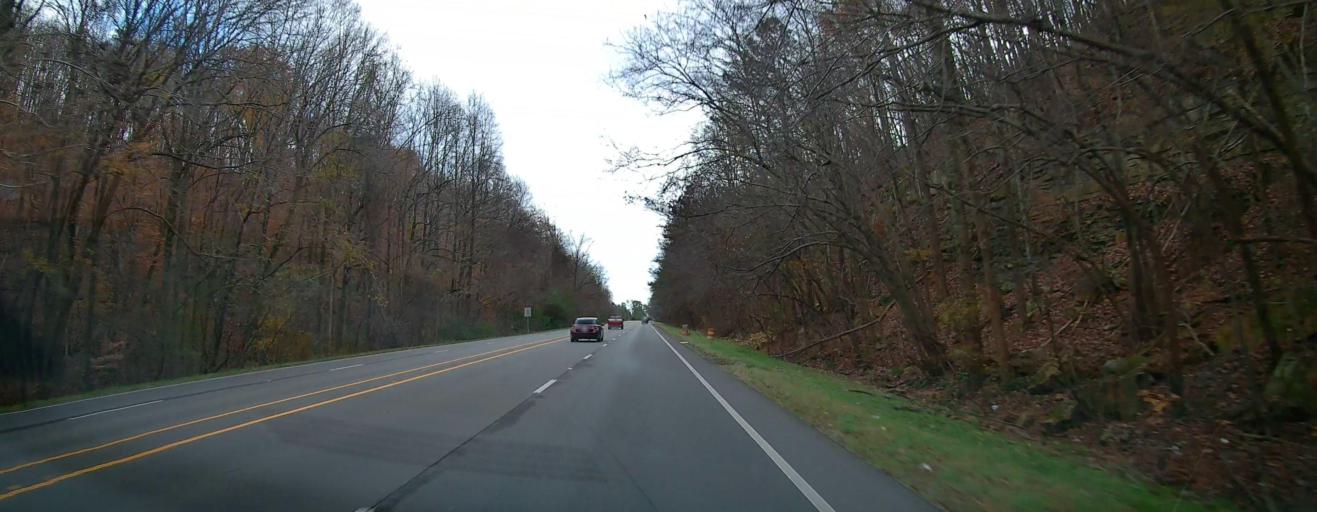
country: US
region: Alabama
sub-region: Morgan County
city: Falkville
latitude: 34.3128
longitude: -86.9986
